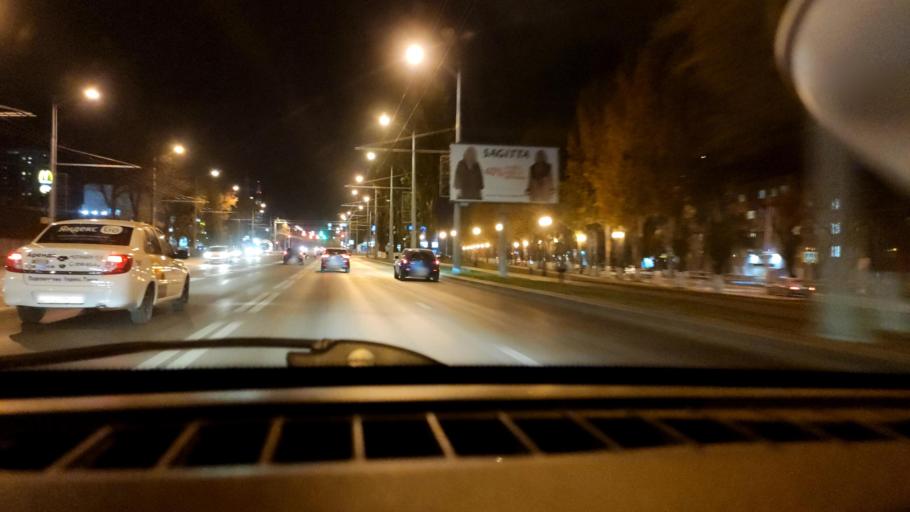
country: RU
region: Samara
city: Samara
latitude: 53.2108
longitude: 50.1770
